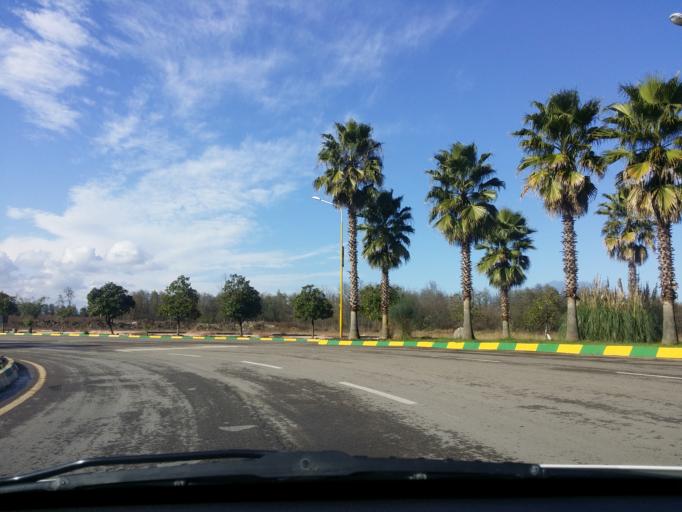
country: IR
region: Mazandaran
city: Chalus
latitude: 36.6836
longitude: 51.3050
